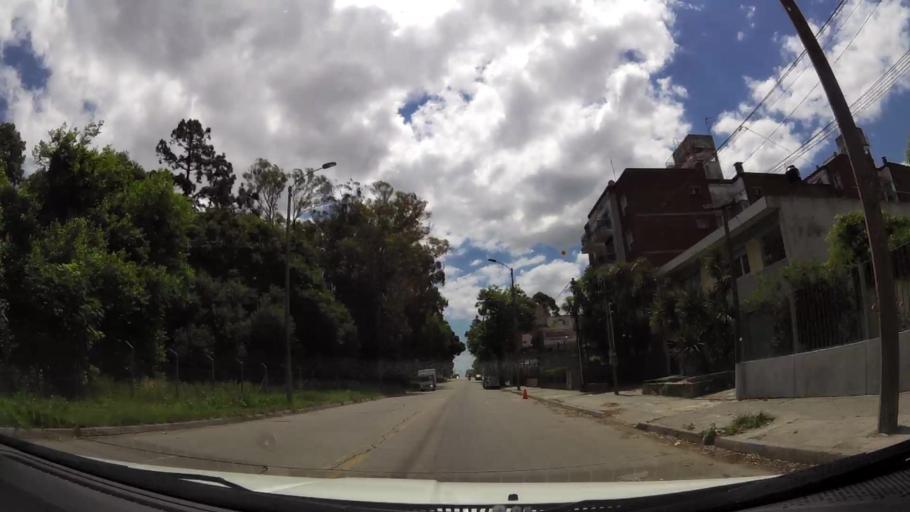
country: UY
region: Montevideo
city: Montevideo
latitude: -34.8362
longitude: -56.2188
